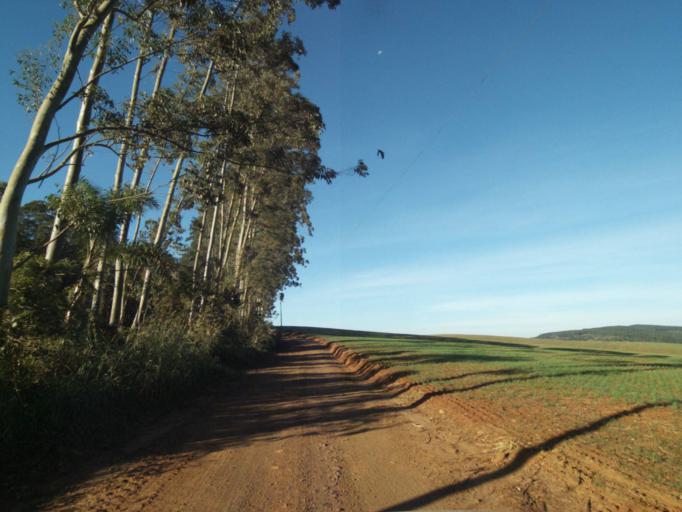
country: BR
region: Parana
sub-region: Telemaco Borba
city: Telemaco Borba
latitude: -24.4799
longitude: -50.5908
